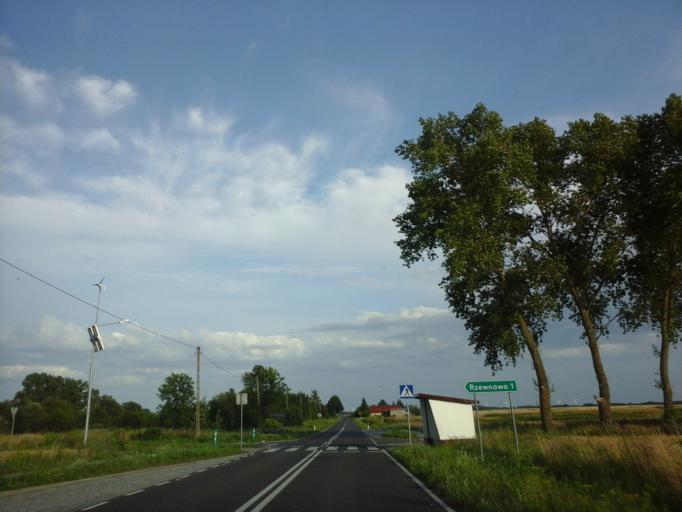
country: PL
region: West Pomeranian Voivodeship
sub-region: Powiat kamienski
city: Kamien Pomorski
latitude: 53.9365
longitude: 14.8167
